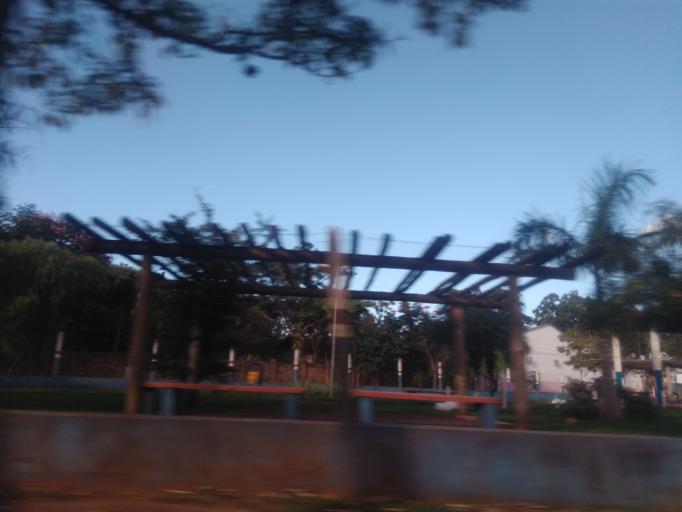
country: BR
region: Mato Grosso do Sul
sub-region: Ponta Pora
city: Ponta Pora
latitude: -22.5212
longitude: -55.7256
